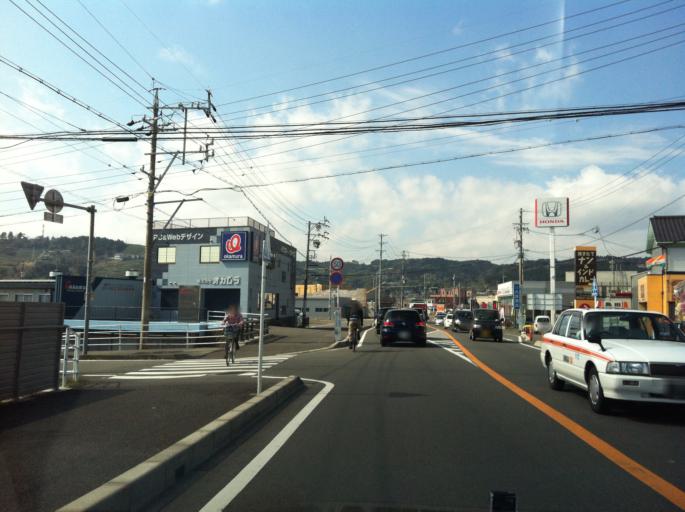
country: JP
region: Shizuoka
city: Kanaya
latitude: 34.8286
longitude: 138.1400
